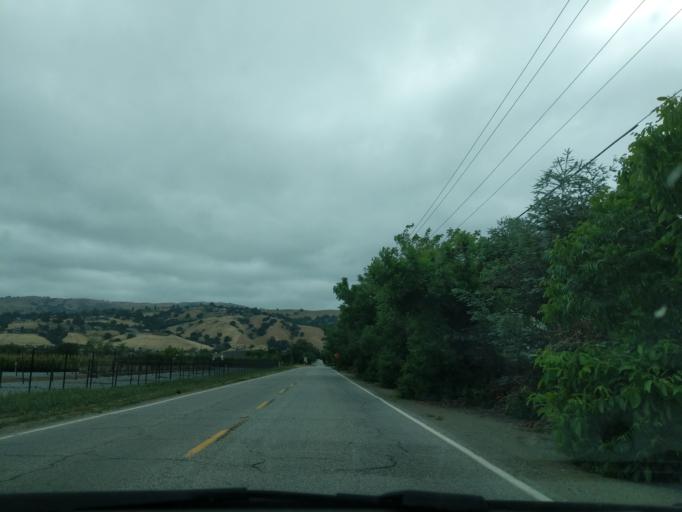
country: US
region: California
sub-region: Santa Clara County
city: San Martin
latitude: 37.1250
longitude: -121.6112
